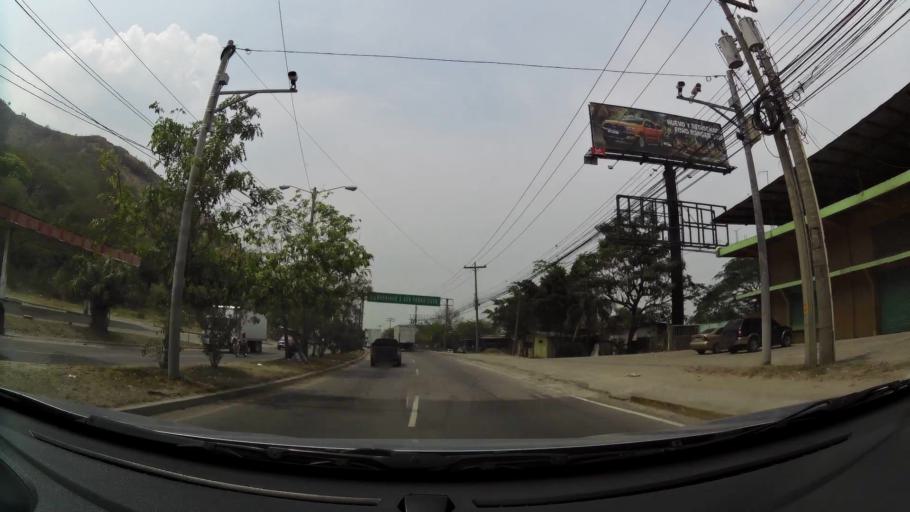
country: HN
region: Cortes
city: Chotepe
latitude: 15.4325
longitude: -88.0210
